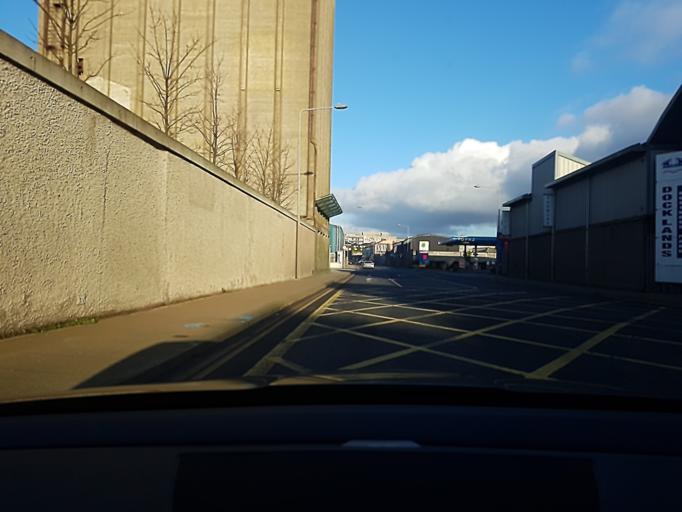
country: IE
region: Munster
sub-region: County Limerick
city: Luimneach
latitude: 52.6579
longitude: -8.6413
